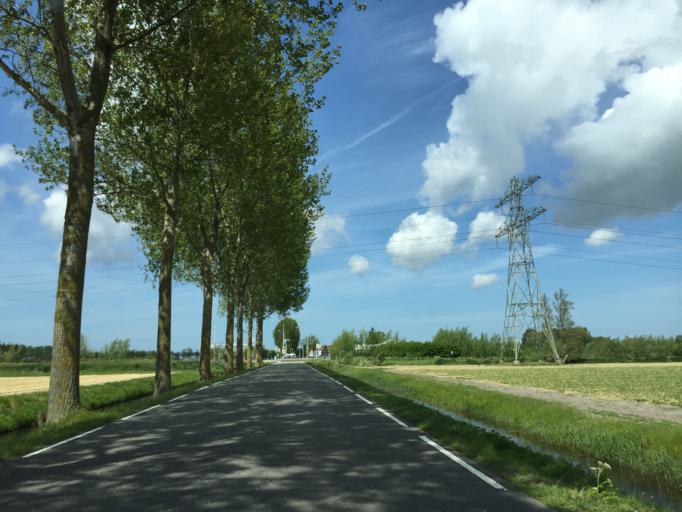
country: NL
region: North Holland
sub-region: Gemeente Haarlemmermeer
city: Hoofddorp
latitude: 52.3434
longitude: 4.6898
